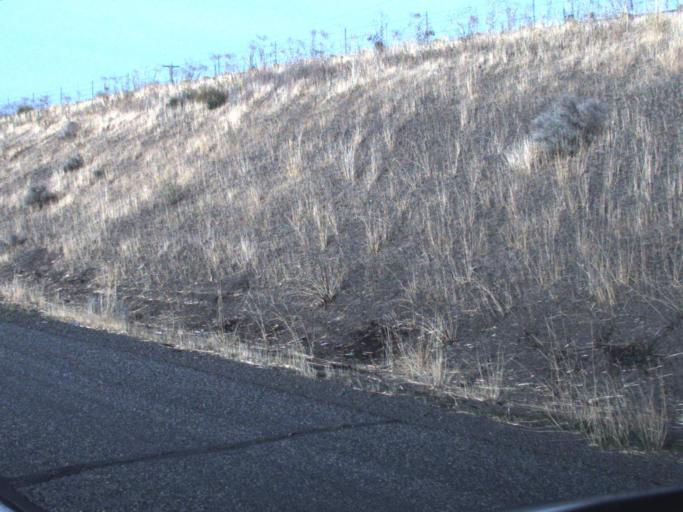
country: US
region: Washington
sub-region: Benton County
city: Highland
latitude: 46.0599
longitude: -119.2235
